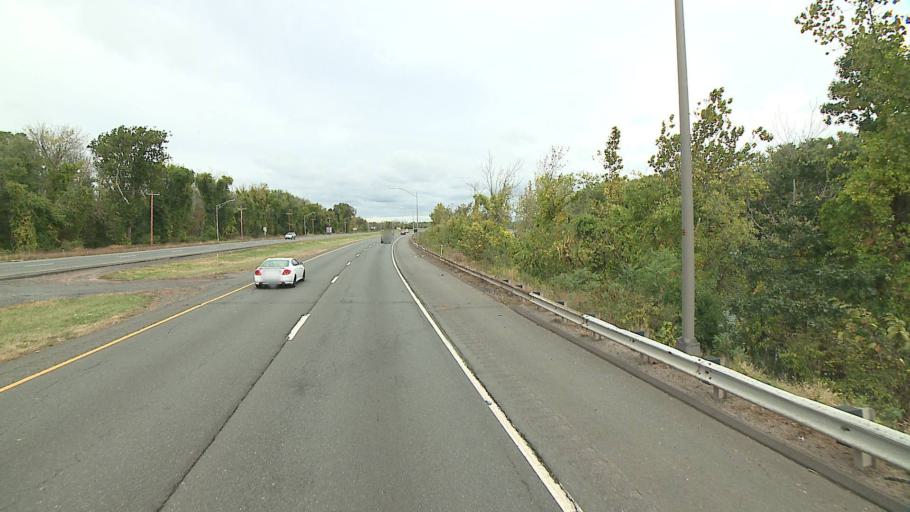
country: US
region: Connecticut
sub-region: Middlesex County
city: Portland
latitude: 41.5765
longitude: -72.6512
